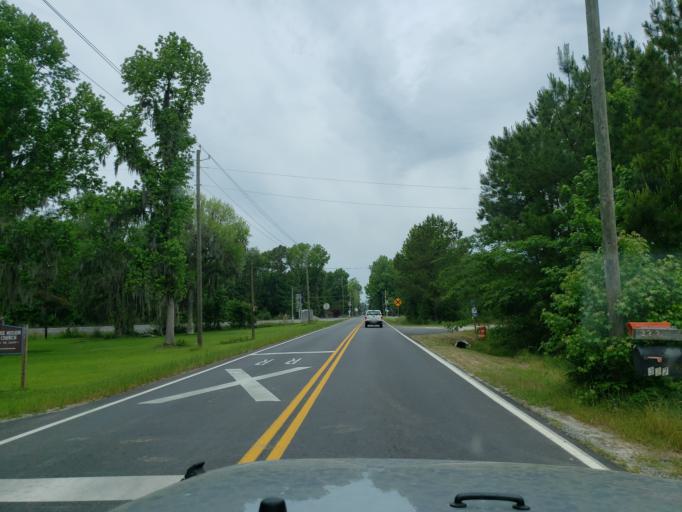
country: US
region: Georgia
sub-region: Chatham County
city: Port Wentworth
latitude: 32.1817
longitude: -81.2113
